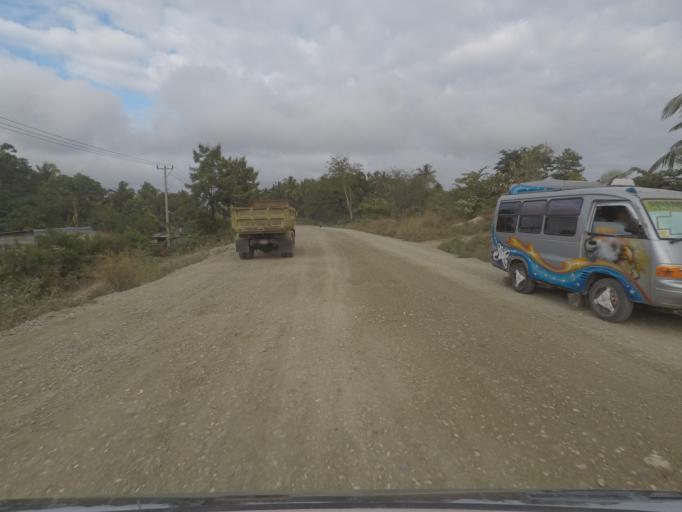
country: TL
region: Baucau
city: Baucau
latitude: -8.5019
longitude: 126.4481
